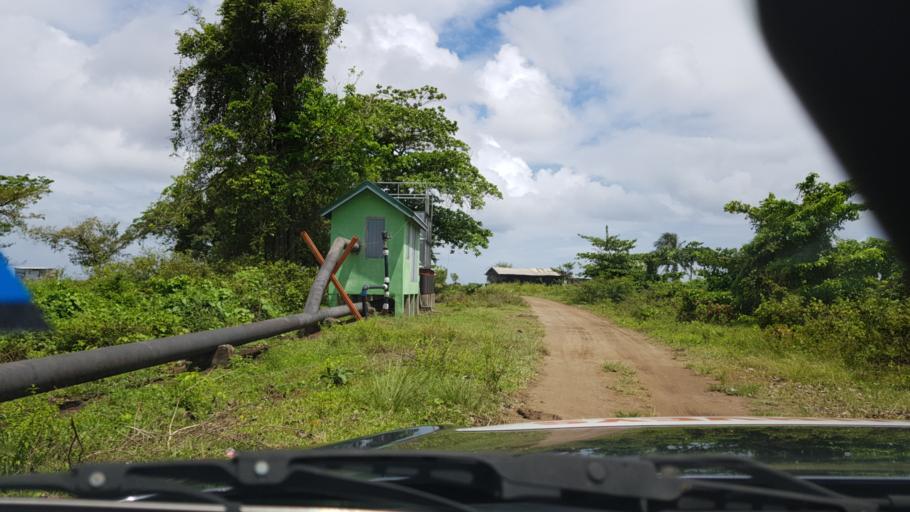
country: LC
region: Anse-la-Raye
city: Anse La Raye
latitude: 13.9572
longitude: -61.0328
